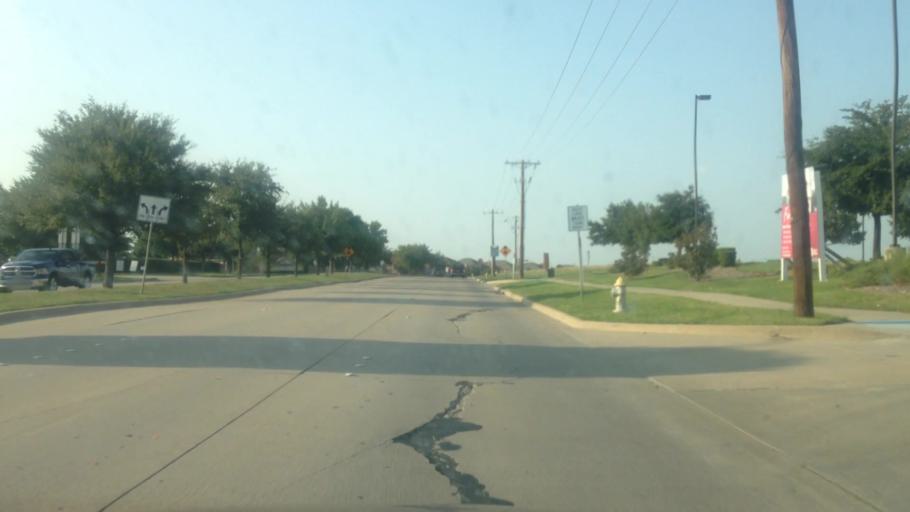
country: US
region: Texas
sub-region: Denton County
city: The Colony
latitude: 33.0624
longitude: -96.9015
